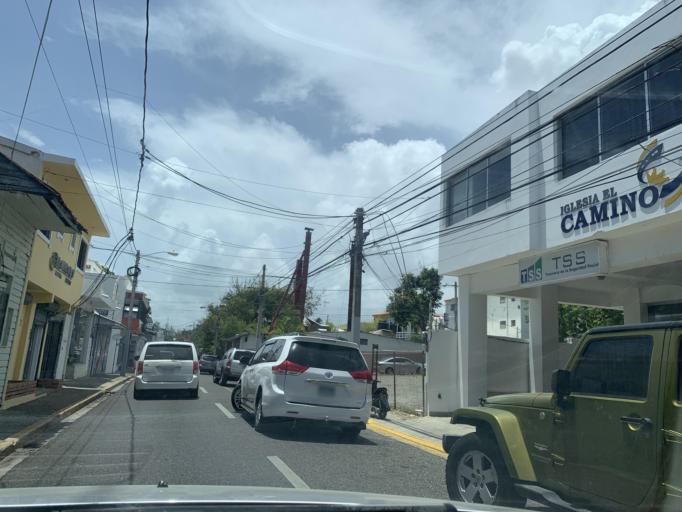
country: DO
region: Puerto Plata
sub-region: Puerto Plata
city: Puerto Plata
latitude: 19.7959
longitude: -70.6891
